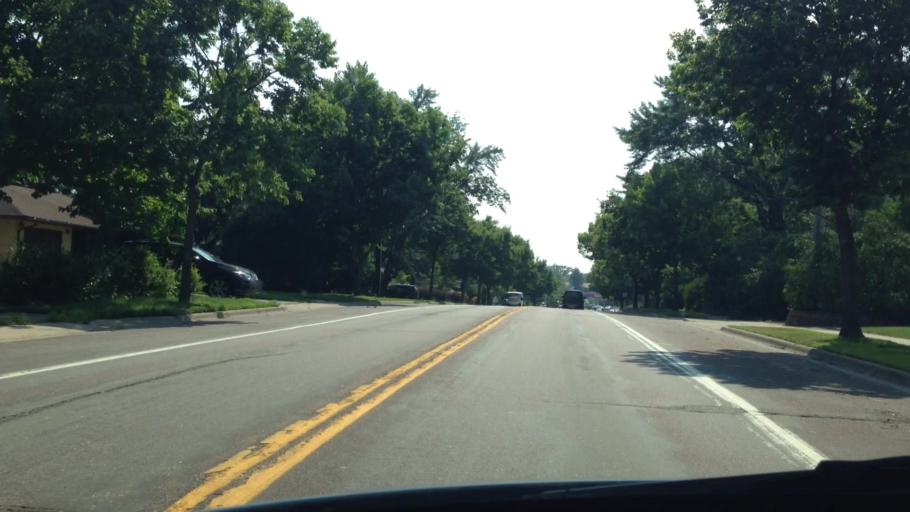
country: US
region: Minnesota
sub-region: Hennepin County
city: Saint Louis Park
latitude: 44.9613
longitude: -93.3674
